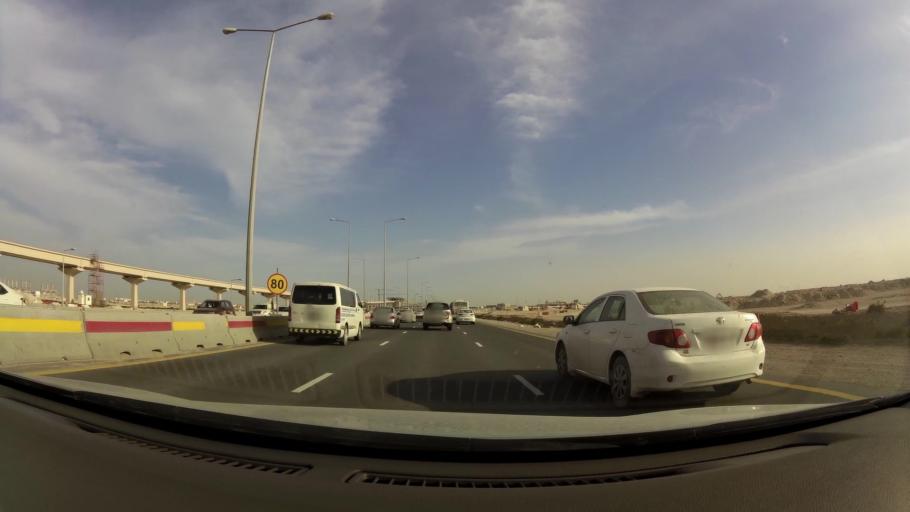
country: QA
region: Al Wakrah
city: Al Wakrah
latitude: 25.2016
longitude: 51.5906
